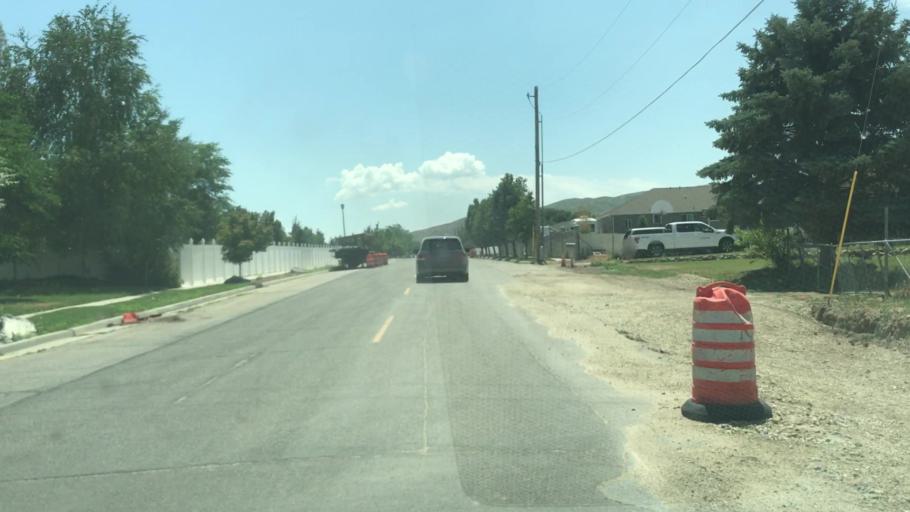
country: US
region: Utah
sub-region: Salt Lake County
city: Bluffdale
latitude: 40.4874
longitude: -111.9484
